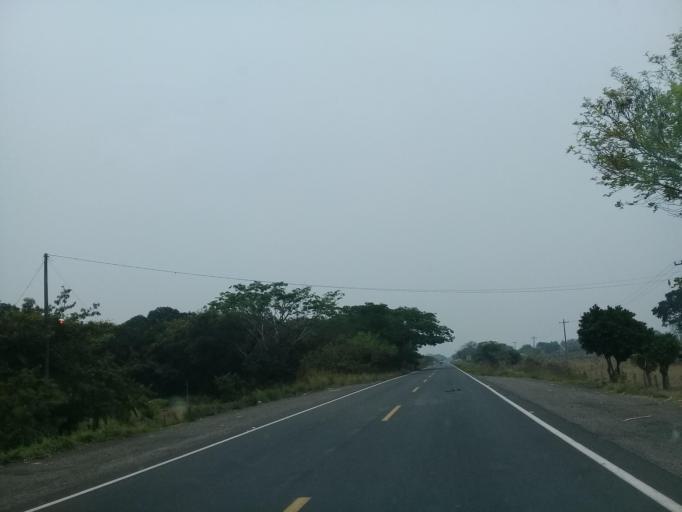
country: MX
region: Veracruz
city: Paso del Toro
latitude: 18.9768
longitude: -96.1770
